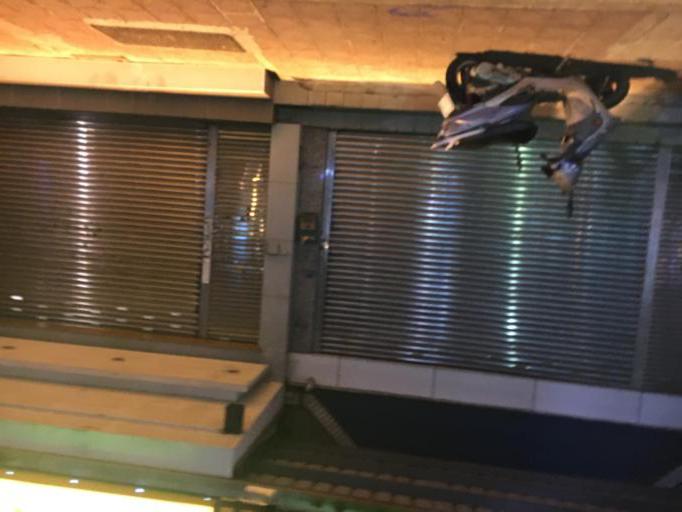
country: TW
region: Taiwan
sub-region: Hsinchu
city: Hsinchu
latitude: 24.7997
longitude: 120.9517
